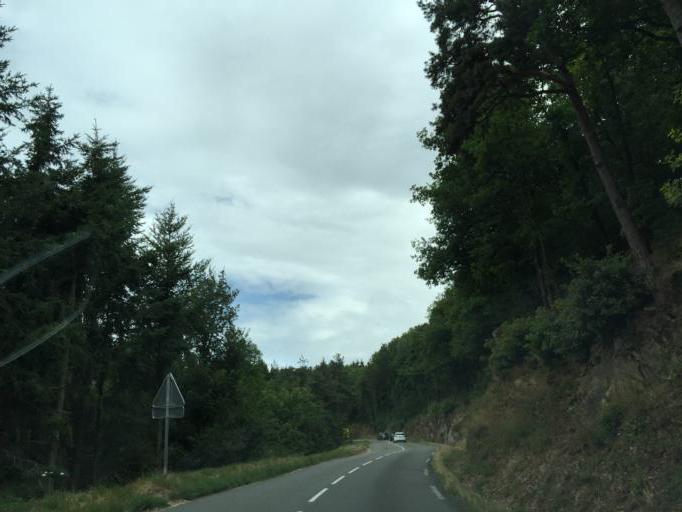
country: FR
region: Rhone-Alpes
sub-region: Departement de la Loire
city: Saint-Paul-en-Cornillon
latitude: 45.4089
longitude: 4.2197
